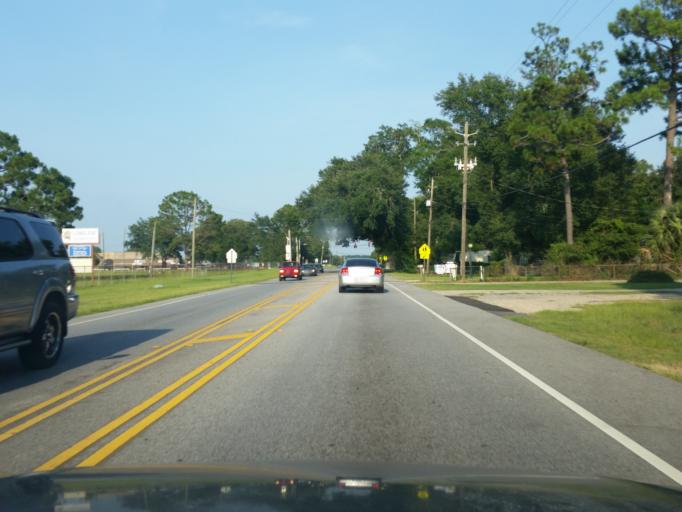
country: US
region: Florida
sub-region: Escambia County
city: Bellview
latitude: 30.4865
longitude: -87.2999
